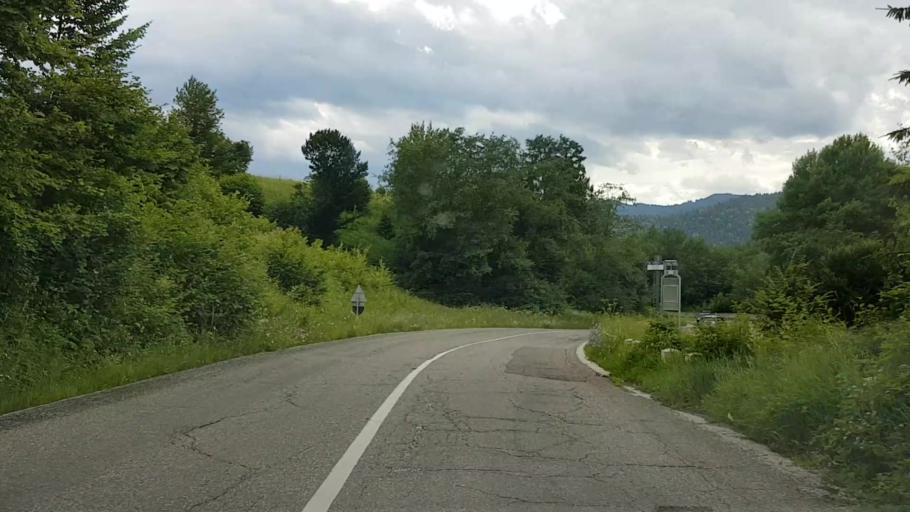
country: RO
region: Neamt
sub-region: Comuna Pangarati
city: Pangarati
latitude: 46.9561
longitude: 26.1246
